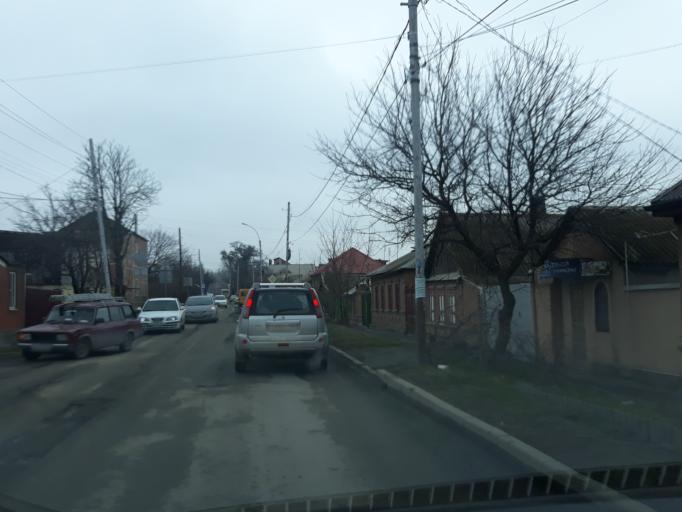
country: RU
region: Rostov
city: Taganrog
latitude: 47.2314
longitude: 38.9250
